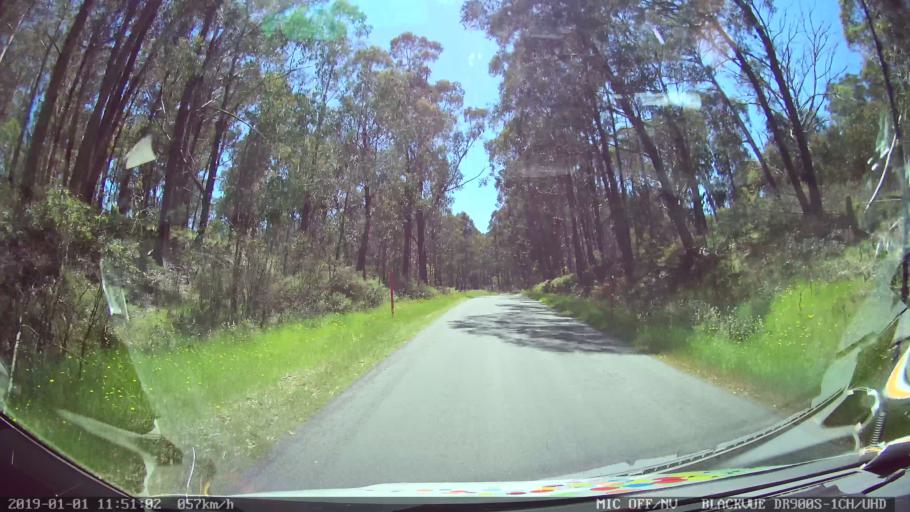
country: AU
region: New South Wales
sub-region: Snowy River
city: Jindabyne
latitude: -35.8880
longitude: 148.4266
